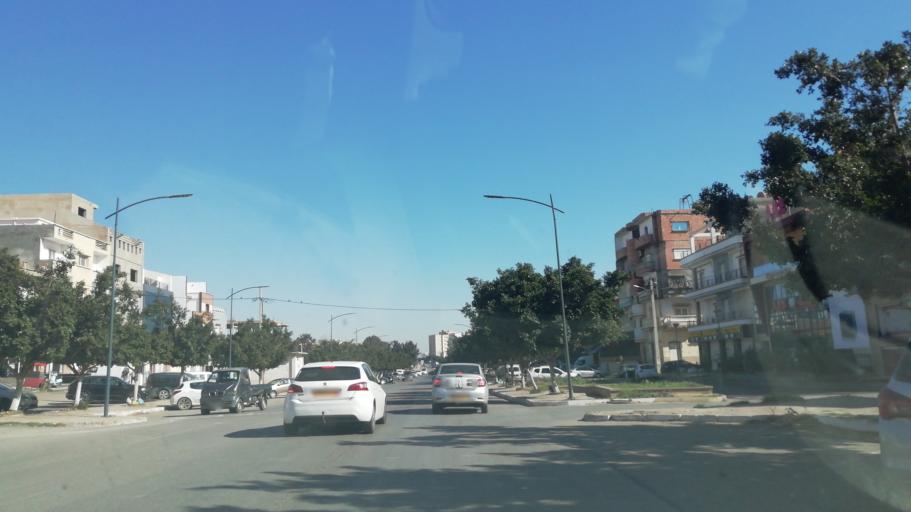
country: DZ
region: Oran
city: Bir el Djir
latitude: 35.7164
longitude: -0.5879
